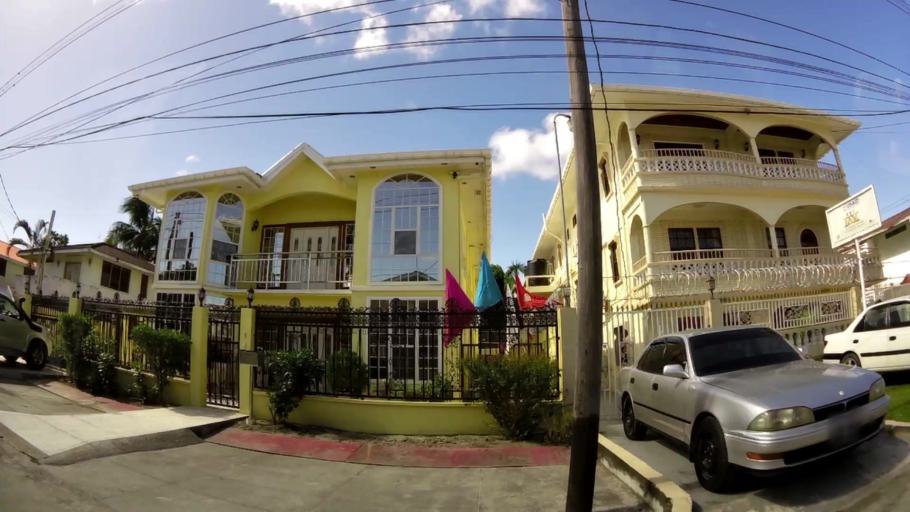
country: GY
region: Demerara-Mahaica
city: Georgetown
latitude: 6.8091
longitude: -58.1393
